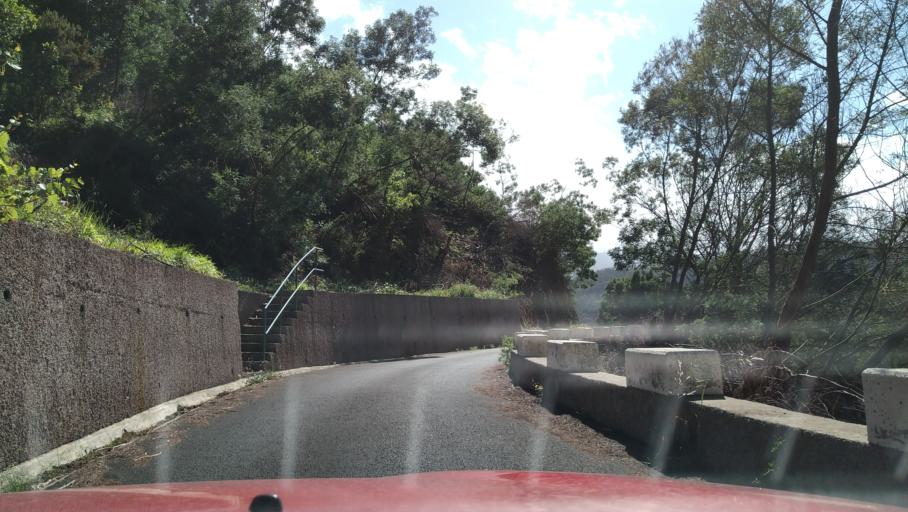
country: PT
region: Madeira
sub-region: Machico
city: Canical
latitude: 32.7392
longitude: -16.7715
